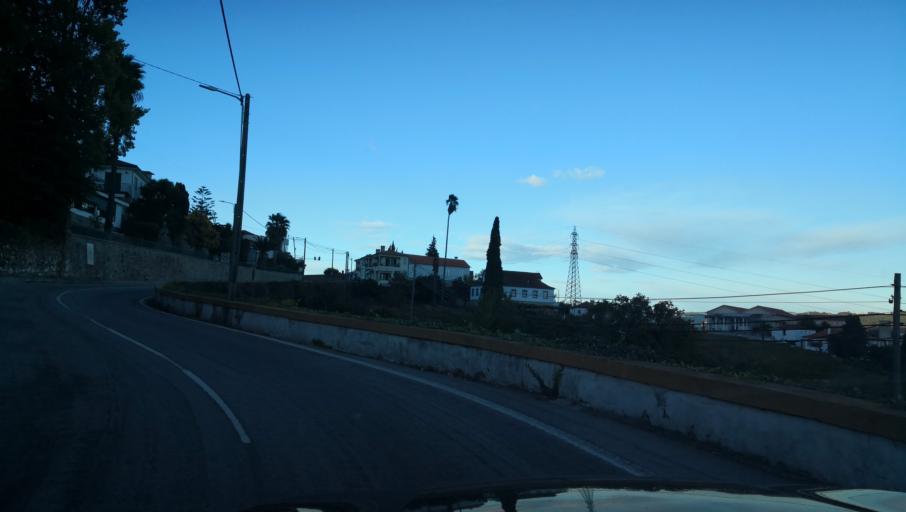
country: PT
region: Vila Real
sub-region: Santa Marta de Penaguiao
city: Santa Marta de Penaguiao
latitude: 41.2545
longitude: -7.7717
